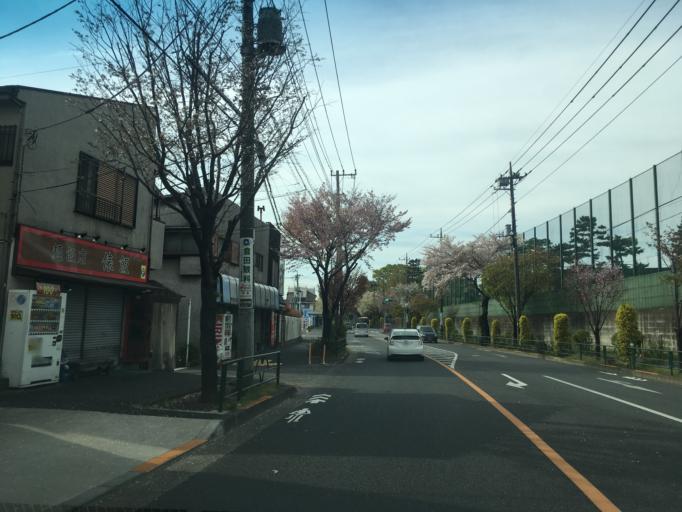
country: JP
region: Tokyo
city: Kokubunji
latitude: 35.7075
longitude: 139.4959
